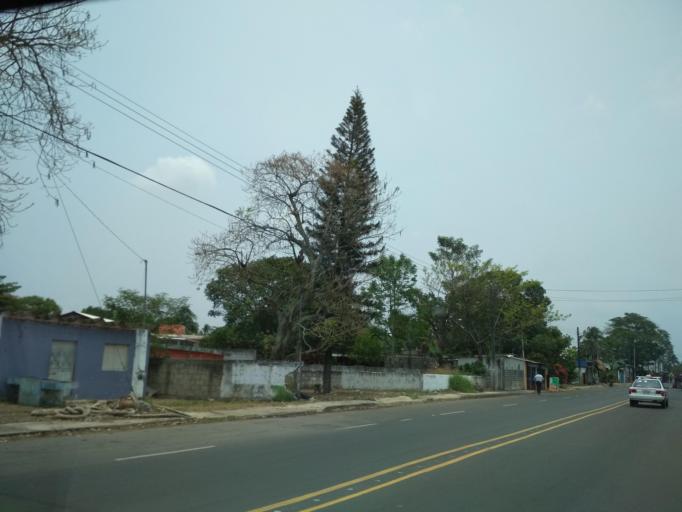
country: MX
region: Veracruz
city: Manlio Fabio Altamirano
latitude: 19.1343
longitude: -96.2980
